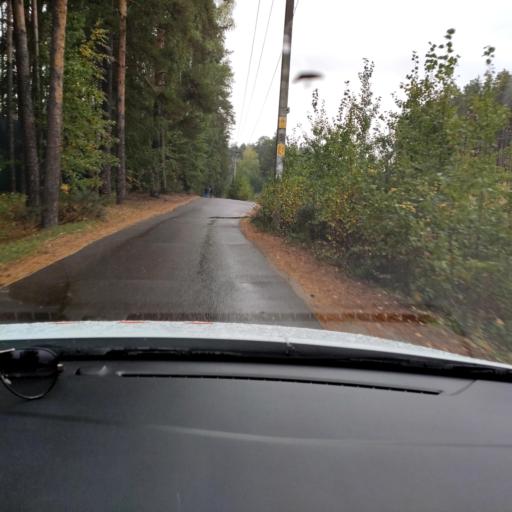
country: RU
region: Tatarstan
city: Verkhniy Uslon
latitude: 55.6408
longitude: 49.0193
